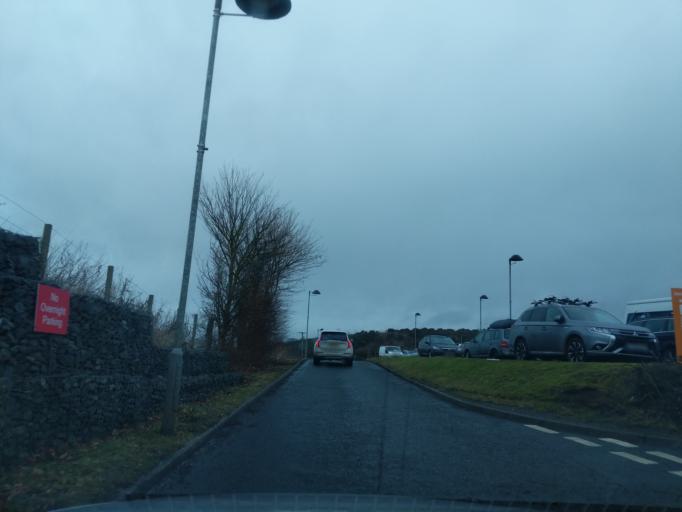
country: GB
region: Scotland
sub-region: Edinburgh
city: Newbridge
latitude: 55.9231
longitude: -3.4007
